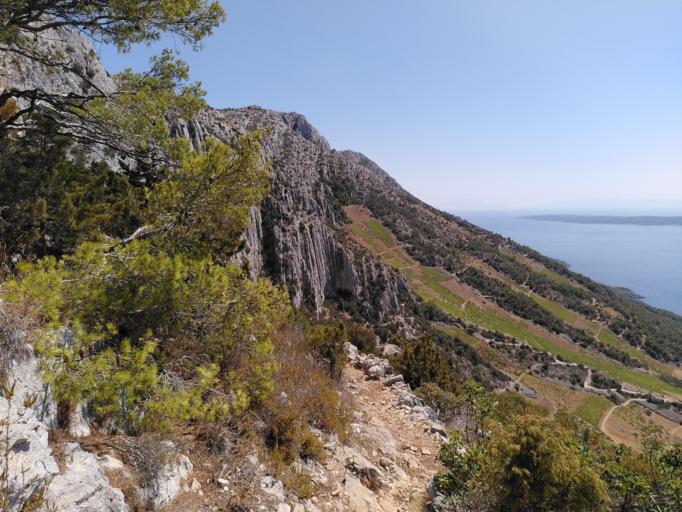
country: HR
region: Splitsko-Dalmatinska
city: Stari Grad
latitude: 43.1443
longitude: 16.5830
